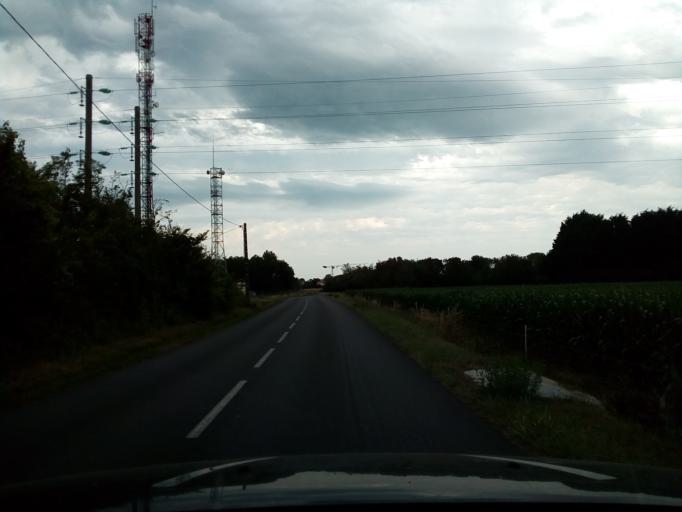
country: FR
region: Poitou-Charentes
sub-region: Departement de la Charente-Maritime
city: Dolus-d'Oleron
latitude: 45.9340
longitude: -1.3133
